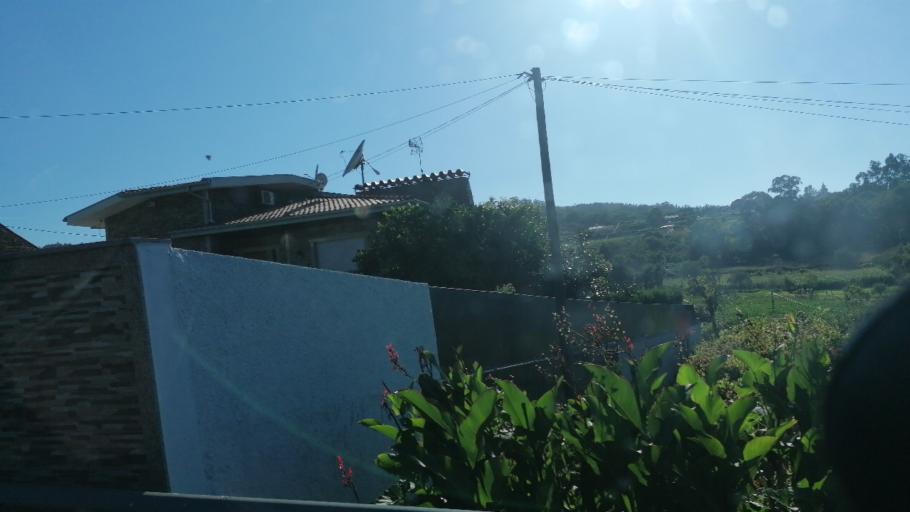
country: PT
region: Porto
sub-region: Santo Tirso
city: Sao Miguel do Couto
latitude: 41.2997
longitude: -8.4710
